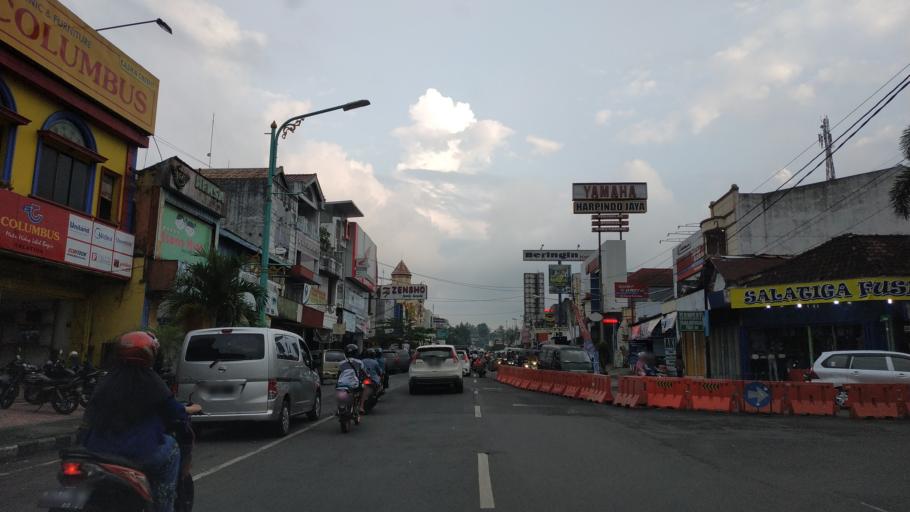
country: ID
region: Central Java
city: Salatiga
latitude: -7.3314
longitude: 110.5051
